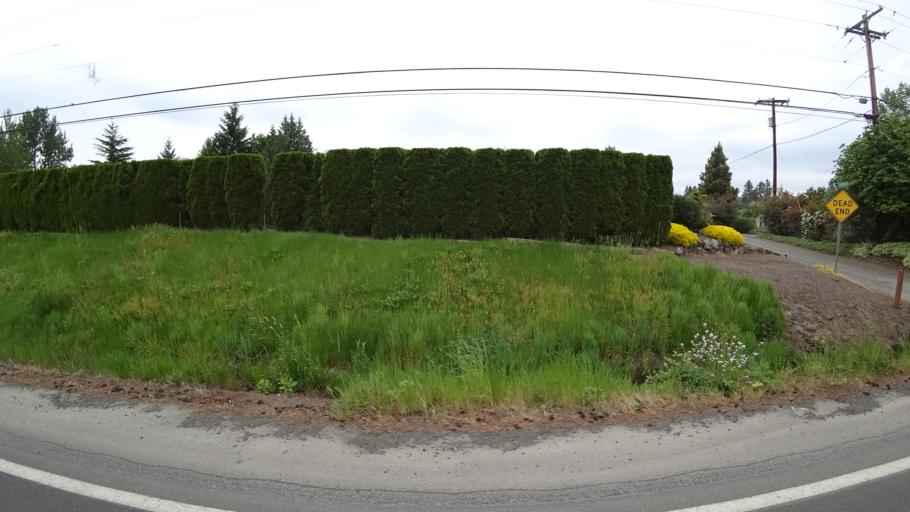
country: US
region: Oregon
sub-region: Washington County
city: Hillsboro
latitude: 45.4946
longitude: -122.9916
